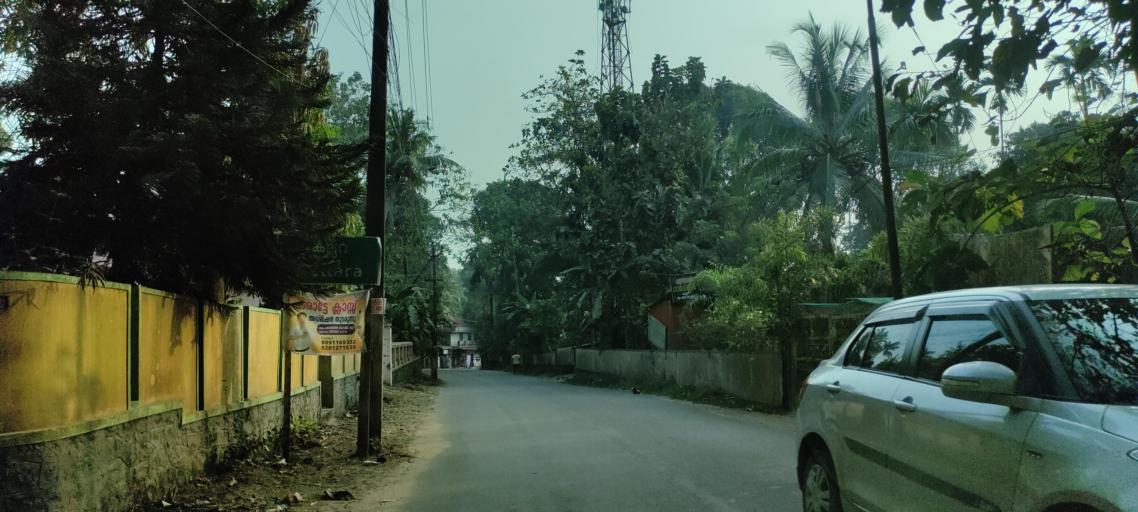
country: IN
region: Kerala
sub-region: Kottayam
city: Vaikam
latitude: 9.7017
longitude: 76.4777
